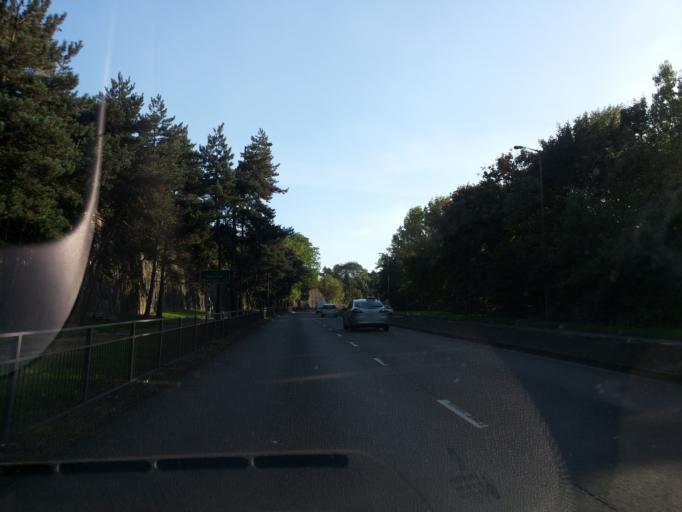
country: GB
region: England
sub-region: Worcestershire
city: Kidderminster
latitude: 52.3849
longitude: -2.2437
